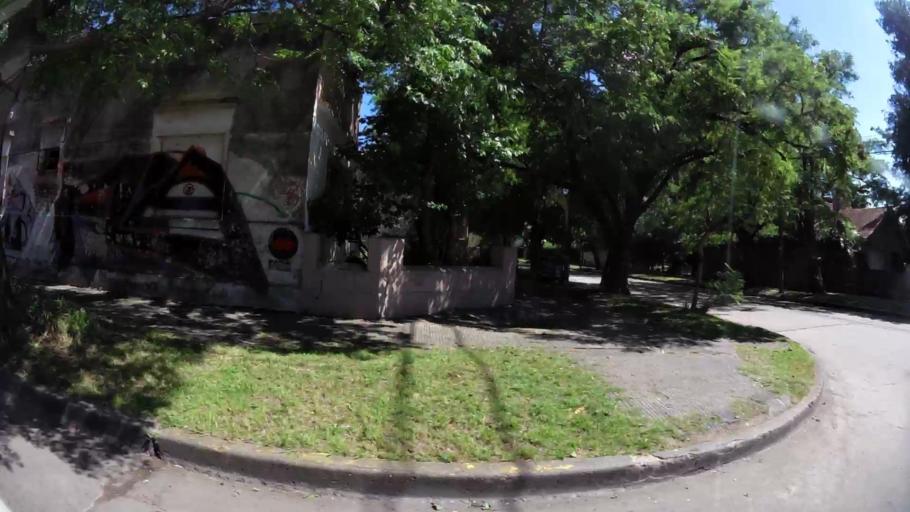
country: AR
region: Buenos Aires
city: Ituzaingo
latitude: -34.6645
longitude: -58.6653
